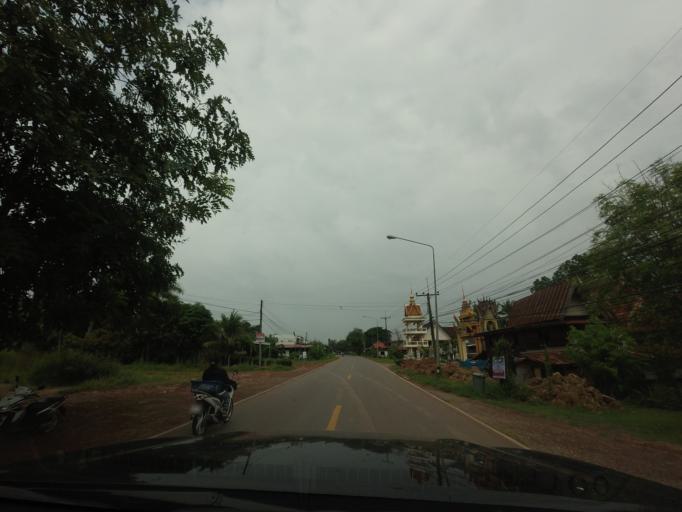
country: TH
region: Nong Khai
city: Tha Bo
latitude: 17.7999
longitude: 102.6658
